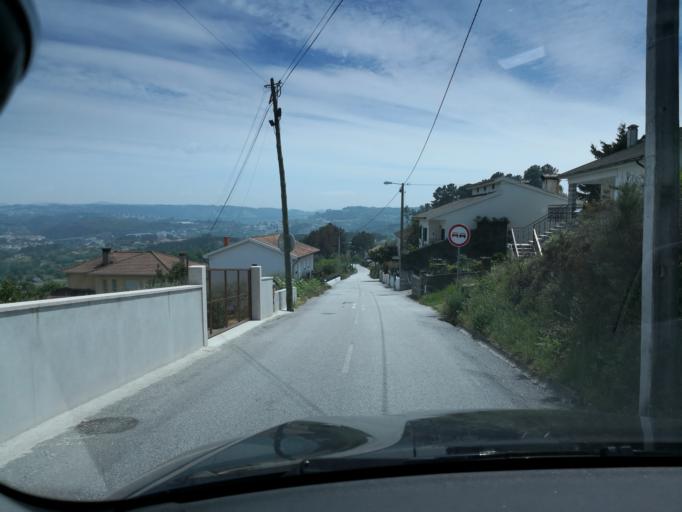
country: PT
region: Vila Real
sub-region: Vila Real
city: Vila Real
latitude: 41.3101
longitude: -7.7809
